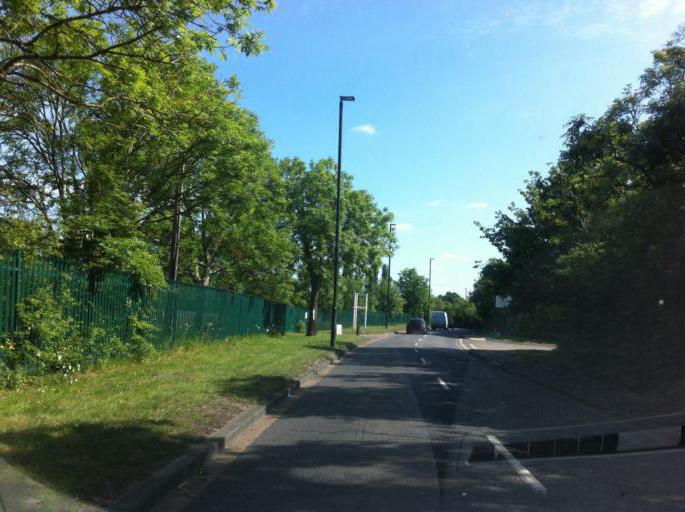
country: GB
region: England
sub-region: Greater London
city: Feltham
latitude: 51.4384
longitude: -0.4543
